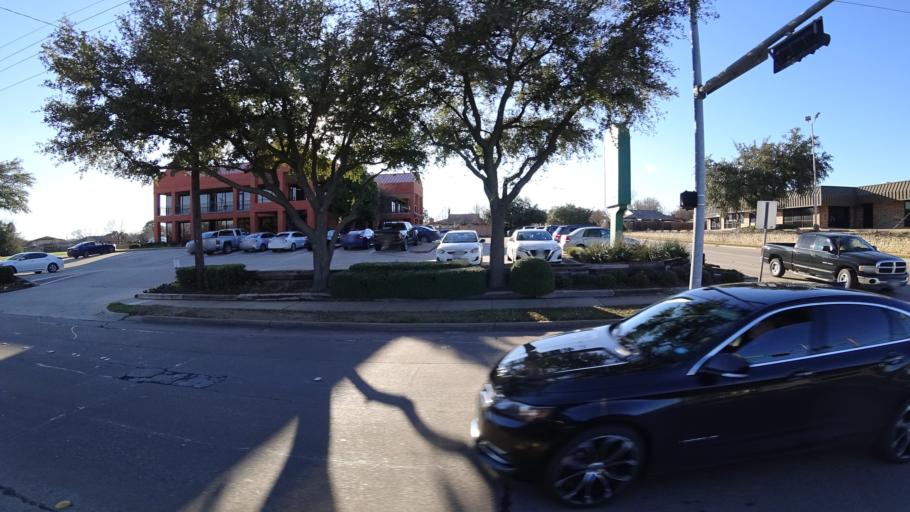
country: US
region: Texas
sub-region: Denton County
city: Lewisville
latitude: 33.0419
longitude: -97.0101
